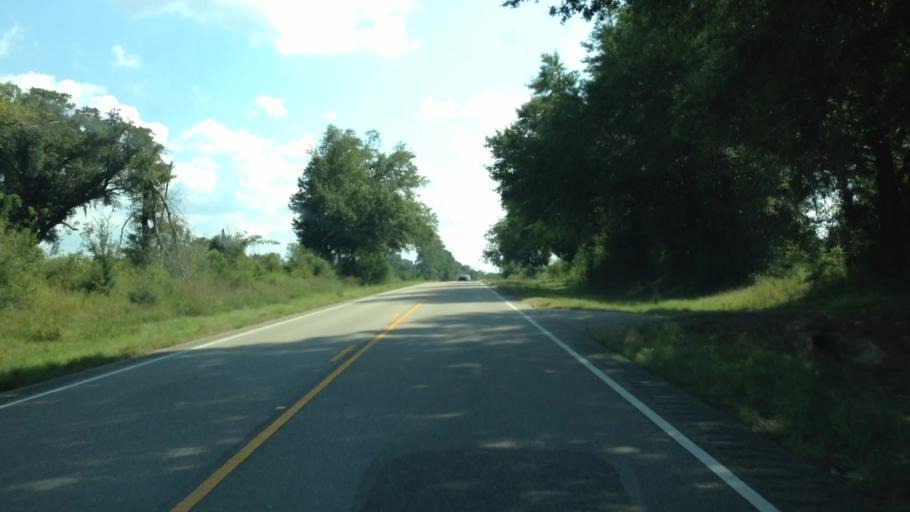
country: US
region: Alabama
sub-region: Covington County
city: Andalusia
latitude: 31.0708
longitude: -86.5752
